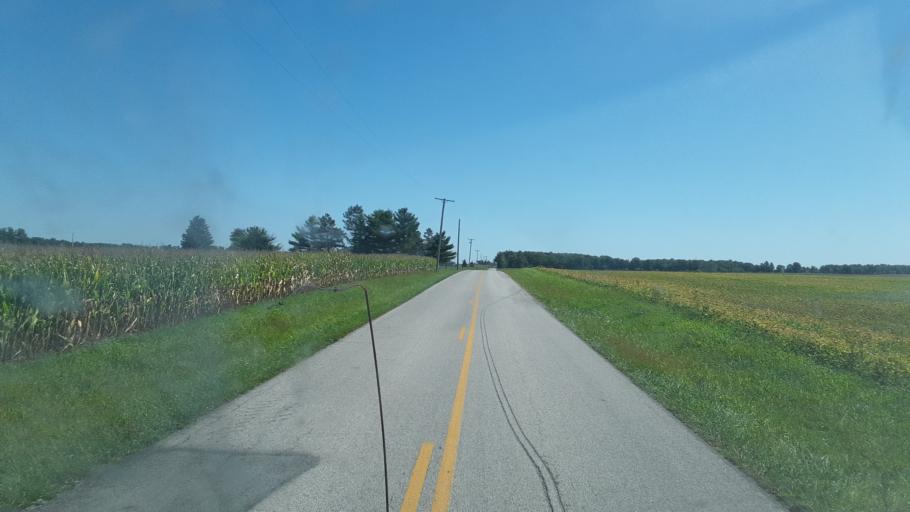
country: US
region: Ohio
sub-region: Sandusky County
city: Mount Carmel
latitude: 41.1613
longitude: -82.9026
